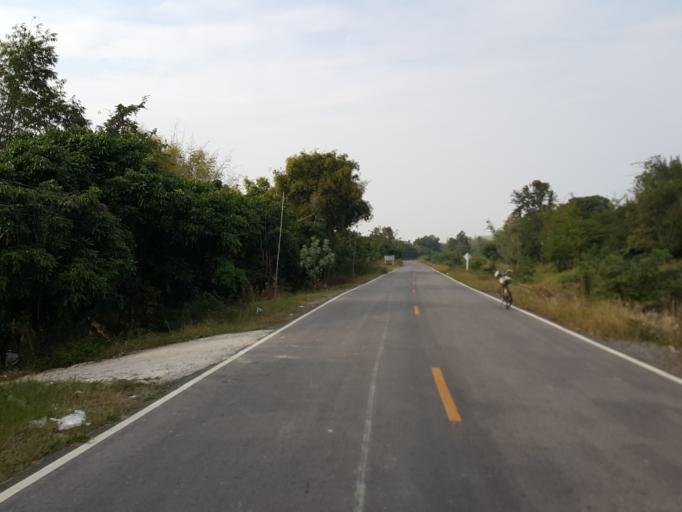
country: TH
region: Chiang Mai
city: San Sai
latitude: 18.8480
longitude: 99.1481
